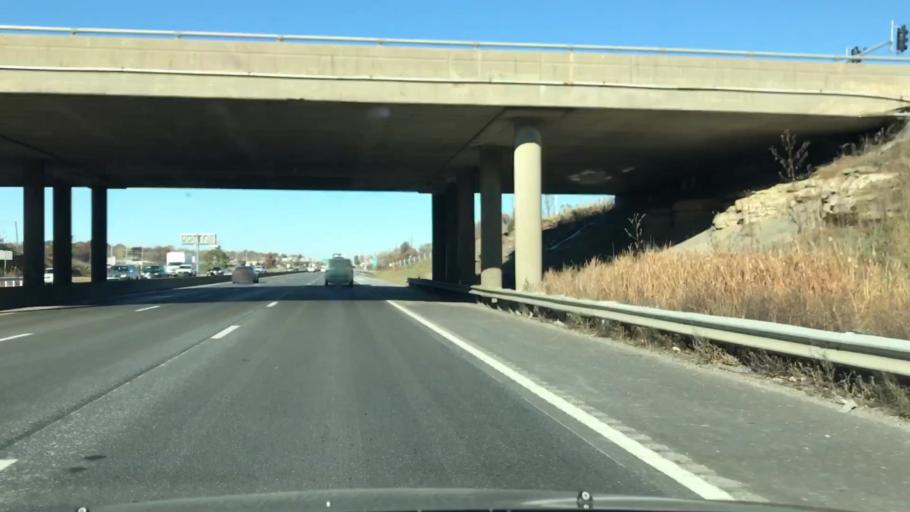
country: US
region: Missouri
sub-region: Jackson County
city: Grandview
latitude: 38.8703
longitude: -94.5263
